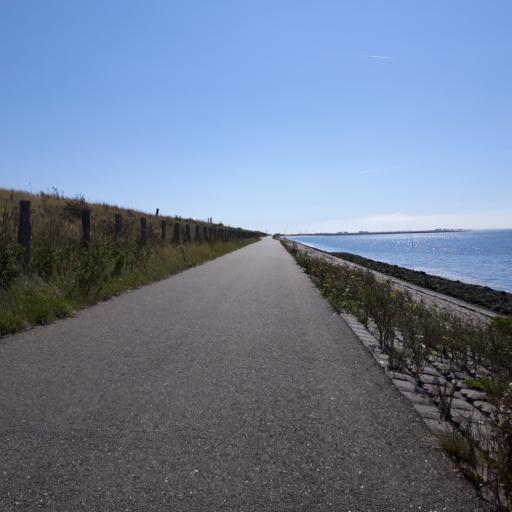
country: NL
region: Zeeland
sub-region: Gemeente Goes
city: Goes
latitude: 51.6247
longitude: 3.9502
